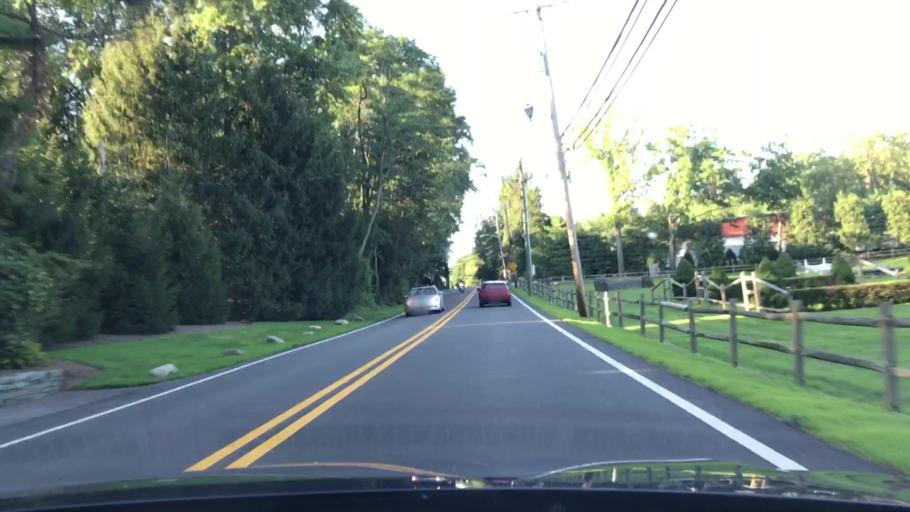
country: US
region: New Jersey
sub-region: Bergen County
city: Northvale
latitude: 41.0016
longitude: -73.9303
